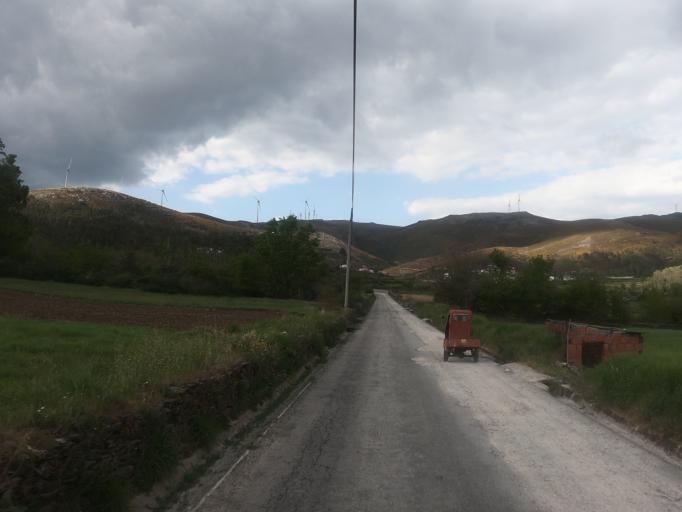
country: PT
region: Vila Real
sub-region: Santa Marta de Penaguiao
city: Santa Marta de Penaguiao
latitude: 41.3091
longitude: -7.8633
